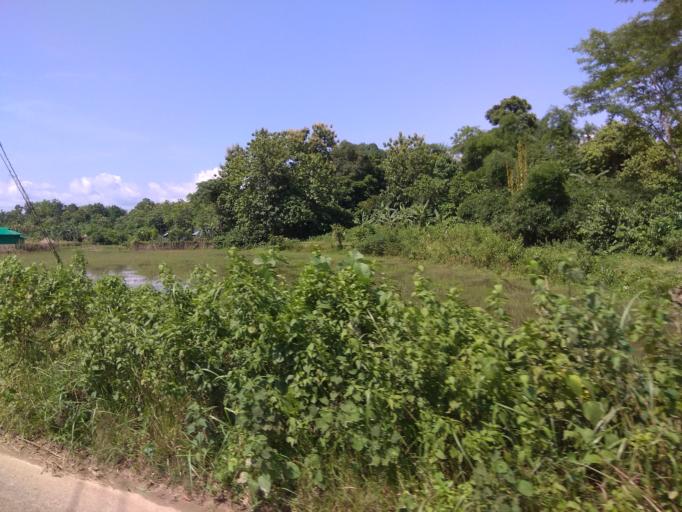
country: BD
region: Chittagong
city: Khagrachhari
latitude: 23.0268
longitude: 92.0146
